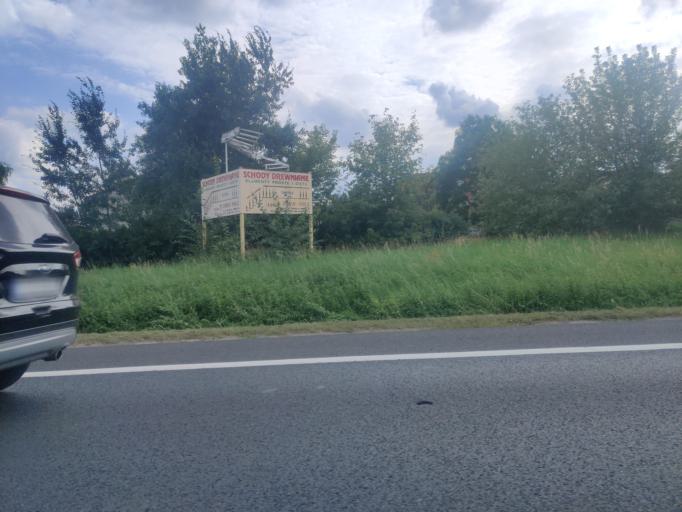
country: PL
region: Greater Poland Voivodeship
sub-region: Konin
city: Konin
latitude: 52.1991
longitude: 18.2918
